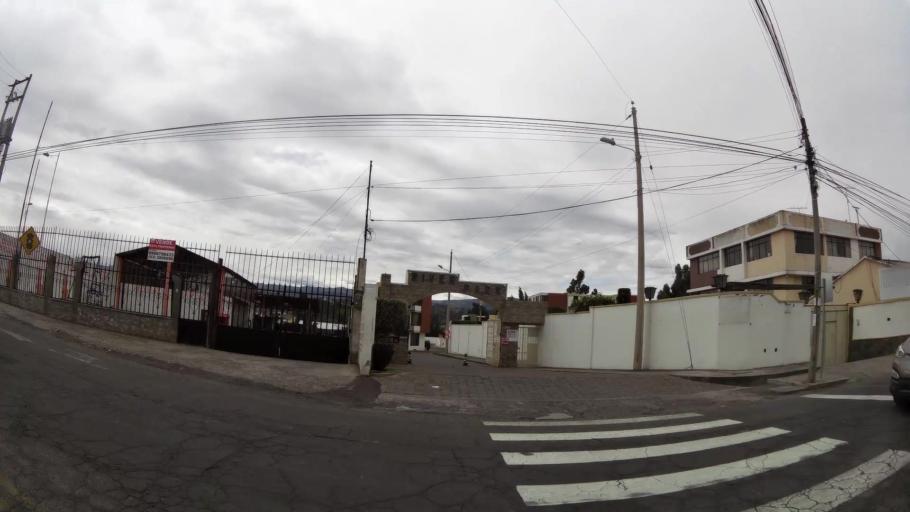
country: EC
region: Cotopaxi
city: Latacunga
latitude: -0.9495
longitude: -78.6103
